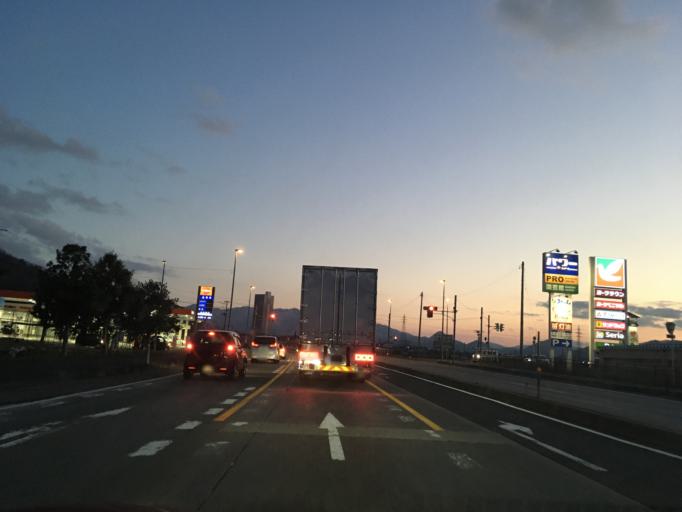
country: JP
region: Yamagata
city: Kaminoyama
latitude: 38.1508
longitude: 140.2913
